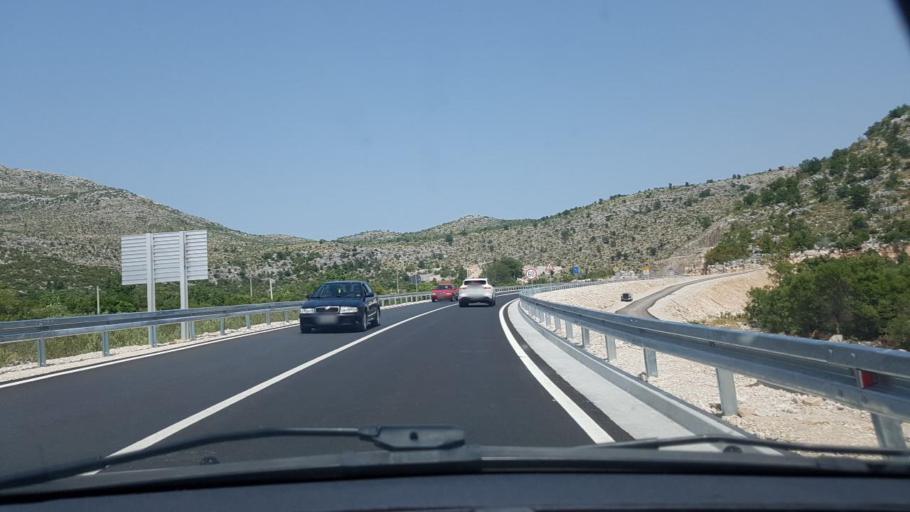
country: HR
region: Dubrovacko-Neretvanska
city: Podgora
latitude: 42.9491
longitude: 17.7792
